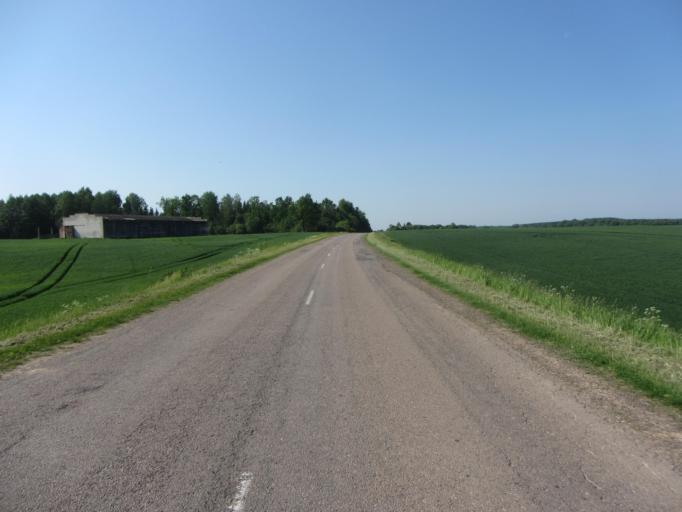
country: LT
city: Kaisiadorys
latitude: 54.9547
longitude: 24.4635
